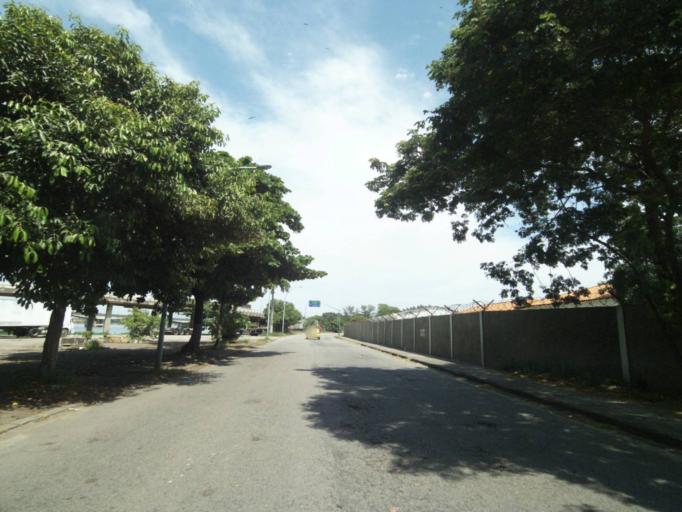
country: BR
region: Rio de Janeiro
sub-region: Rio De Janeiro
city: Rio de Janeiro
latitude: -22.8334
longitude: -43.2413
